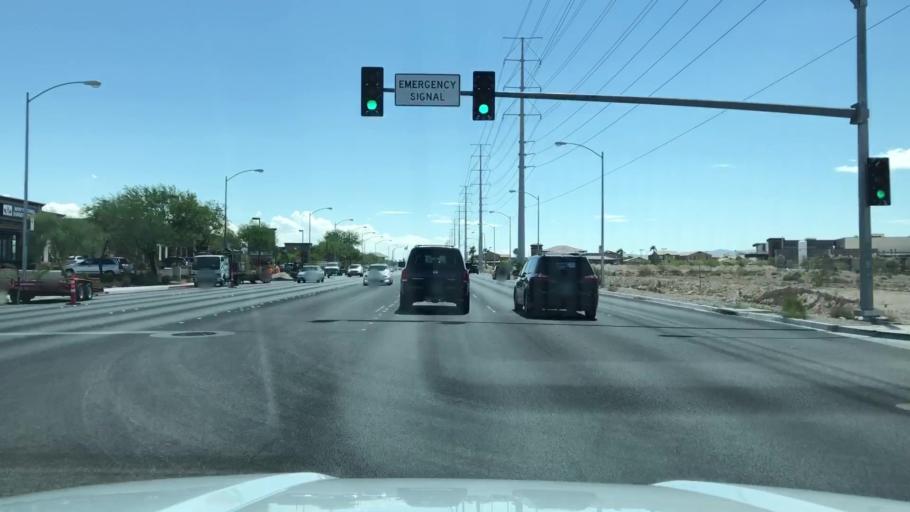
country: US
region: Nevada
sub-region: Clark County
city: Spring Valley
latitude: 36.0815
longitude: -115.2794
